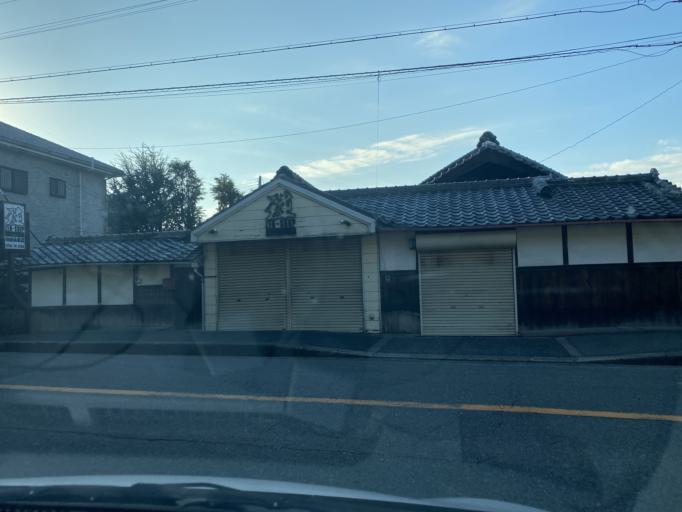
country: JP
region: Osaka
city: Izumi
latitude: 34.4256
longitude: 135.4391
